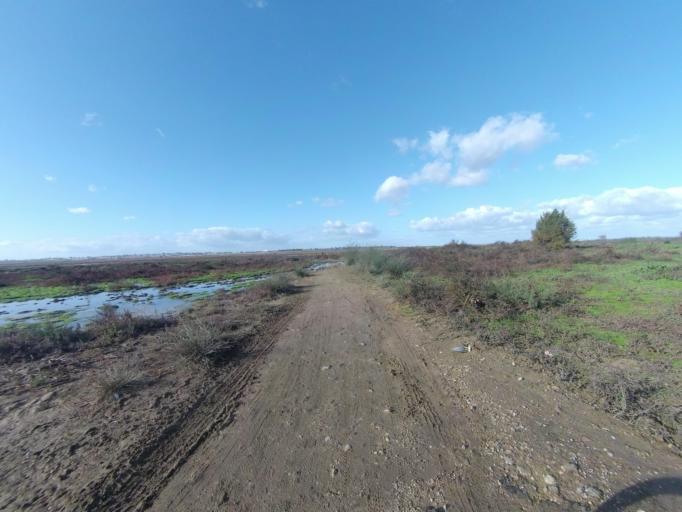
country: ES
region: Andalusia
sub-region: Provincia de Huelva
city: Palos de la Frontera
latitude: 37.2484
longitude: -6.8835
